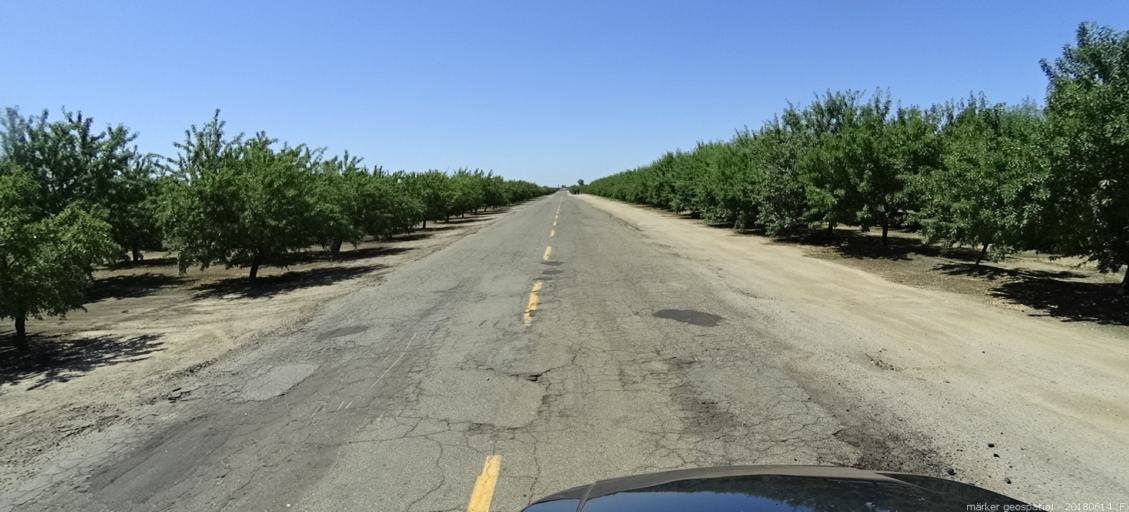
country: US
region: California
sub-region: Madera County
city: Fairmead
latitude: 36.9914
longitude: -120.1661
